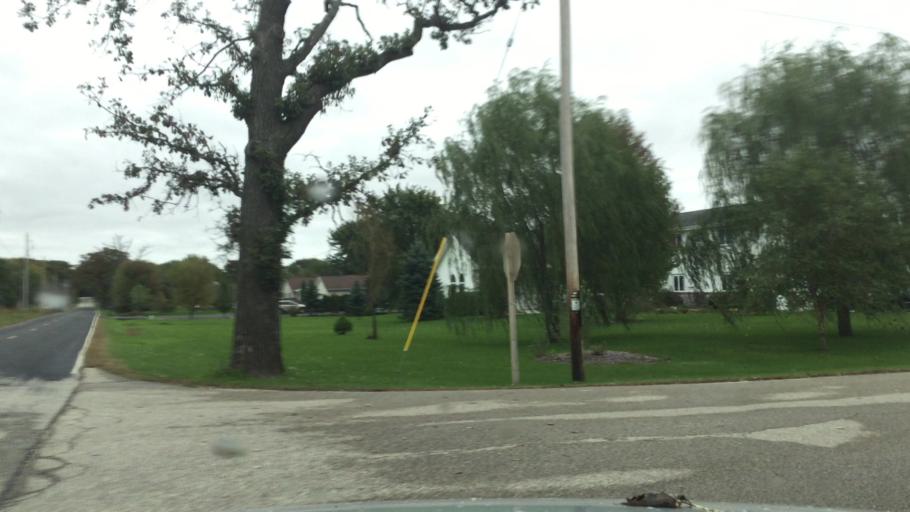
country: US
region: Wisconsin
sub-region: Racine County
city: Eagle Lake
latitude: 42.7567
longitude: -88.1555
